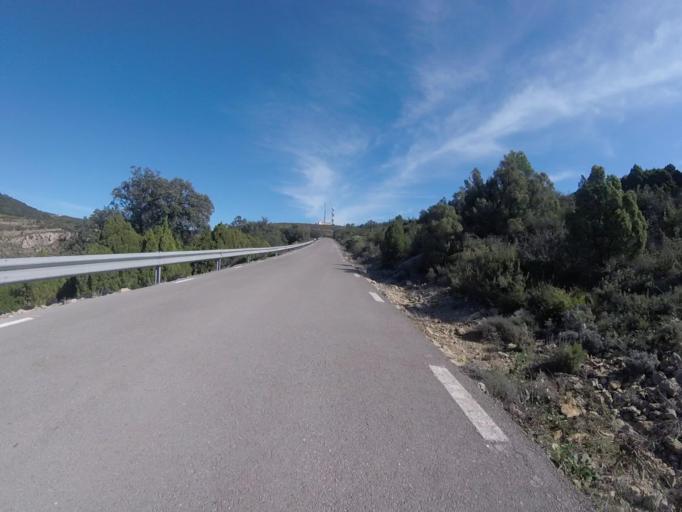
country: ES
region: Valencia
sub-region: Provincia de Castello
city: Sarratella
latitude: 40.2968
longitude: 0.0273
